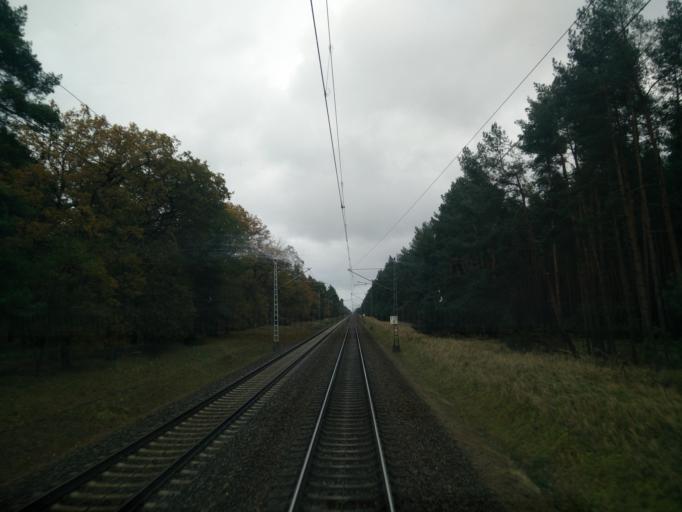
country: DE
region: Brandenburg
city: Bad Wilsnack
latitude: 52.9497
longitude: 11.9736
